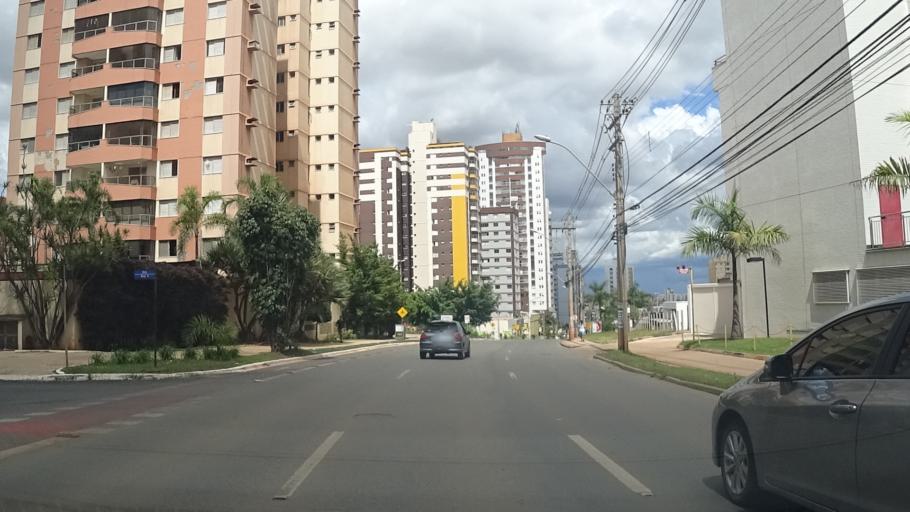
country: BR
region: Federal District
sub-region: Brasilia
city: Brasilia
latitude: -15.8373
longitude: -48.0143
